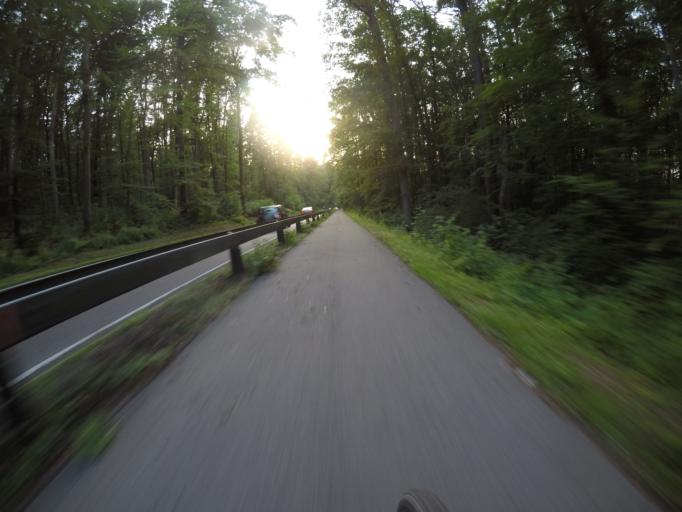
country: DE
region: Baden-Wuerttemberg
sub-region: Regierungsbezirk Stuttgart
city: Steinenbronn
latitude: 48.6733
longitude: 9.1249
